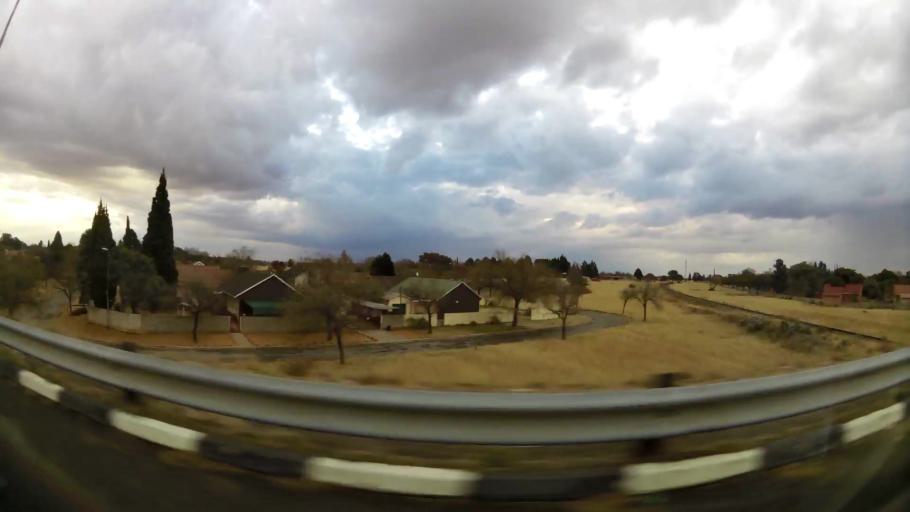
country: ZA
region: Orange Free State
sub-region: Lejweleputswa District Municipality
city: Welkom
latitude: -27.9597
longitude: 26.7263
